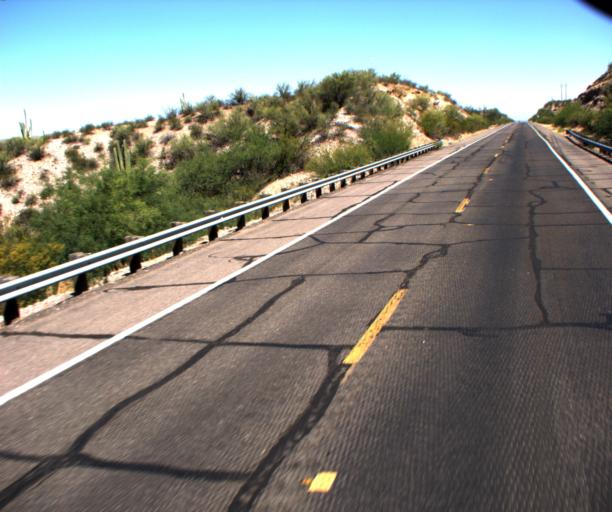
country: US
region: Arizona
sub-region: Pinal County
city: Mammoth
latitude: 32.7568
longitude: -110.6495
